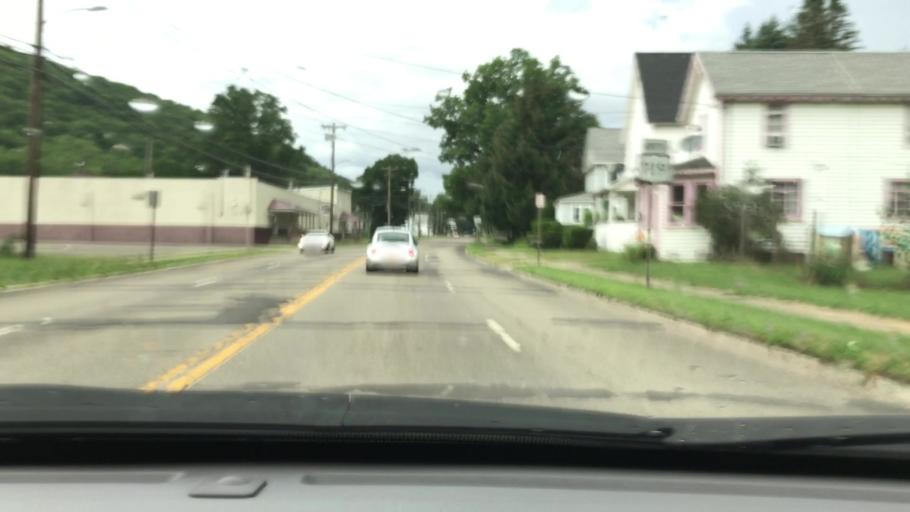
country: US
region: New York
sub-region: Cattaraugus County
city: Salamanca
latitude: 42.1625
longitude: -78.6958
